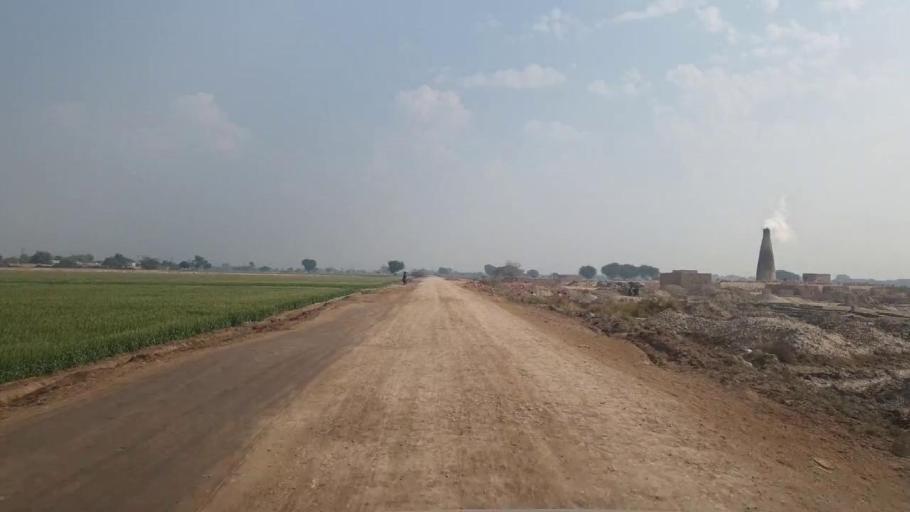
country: PK
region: Sindh
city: Hala
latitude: 25.7839
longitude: 68.4263
